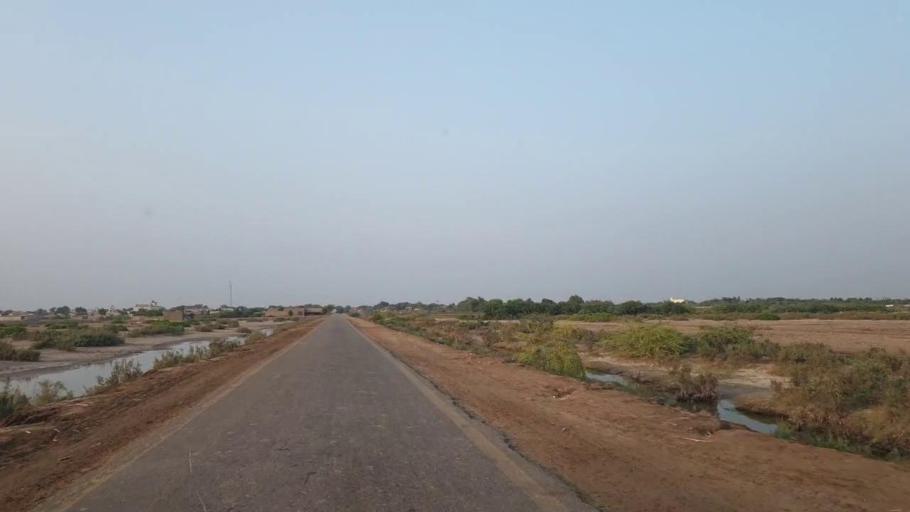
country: PK
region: Sindh
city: Tando Ghulam Ali
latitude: 25.1379
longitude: 68.9587
